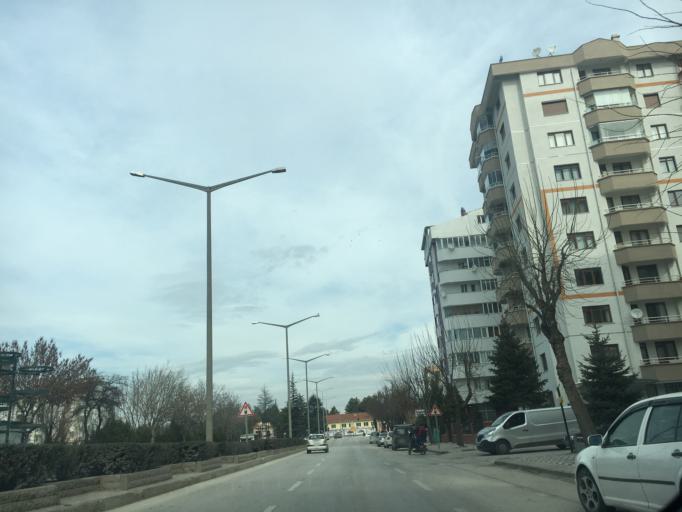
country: TR
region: Eskisehir
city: Eskisehir
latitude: 39.7722
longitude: 30.5012
